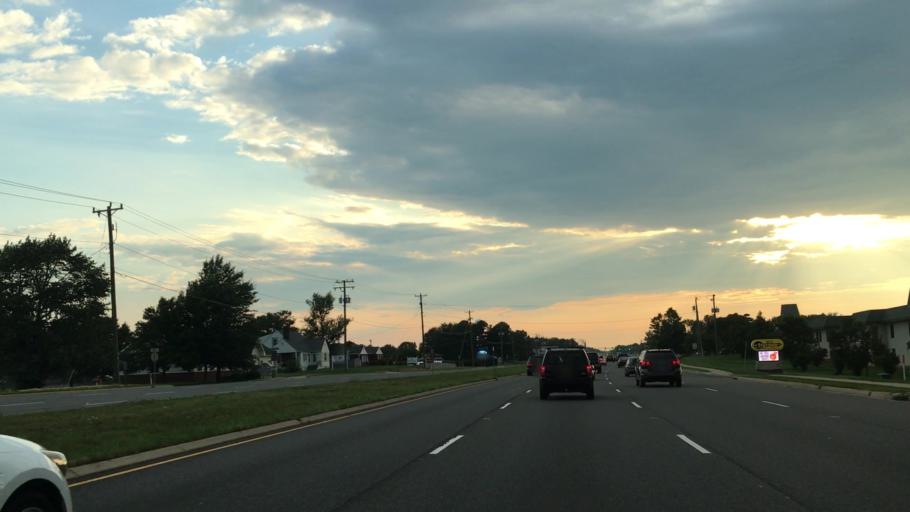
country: US
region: Virginia
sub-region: Stafford County
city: Falmouth
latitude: 38.2892
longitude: -77.5413
